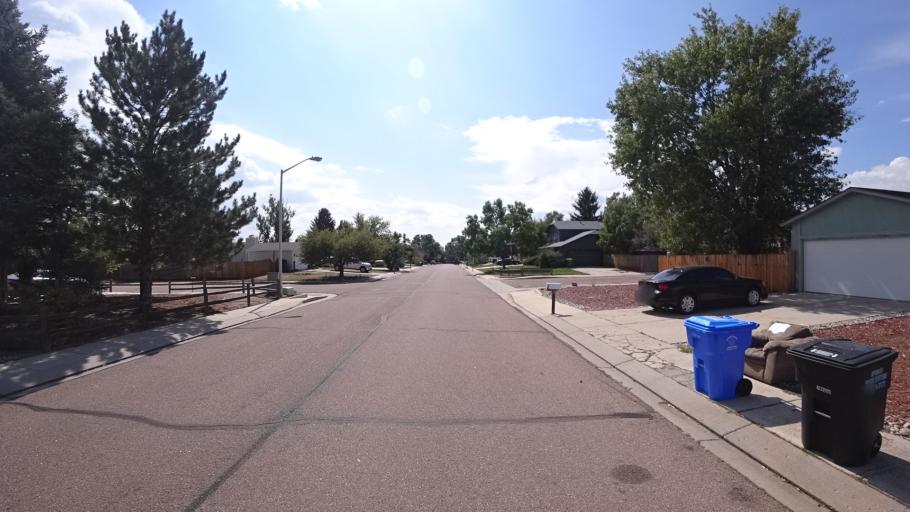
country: US
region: Colorado
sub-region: El Paso County
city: Cimarron Hills
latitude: 38.8630
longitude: -104.7251
